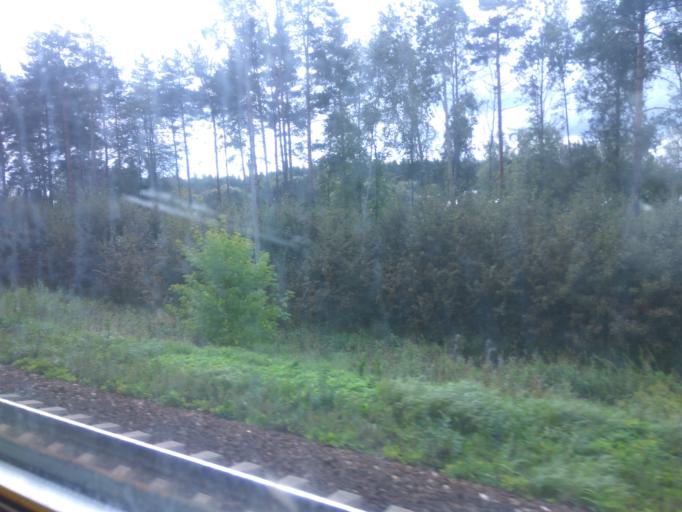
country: RU
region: Moskovskaya
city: Malyshevo
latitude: 55.4863
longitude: 38.3930
